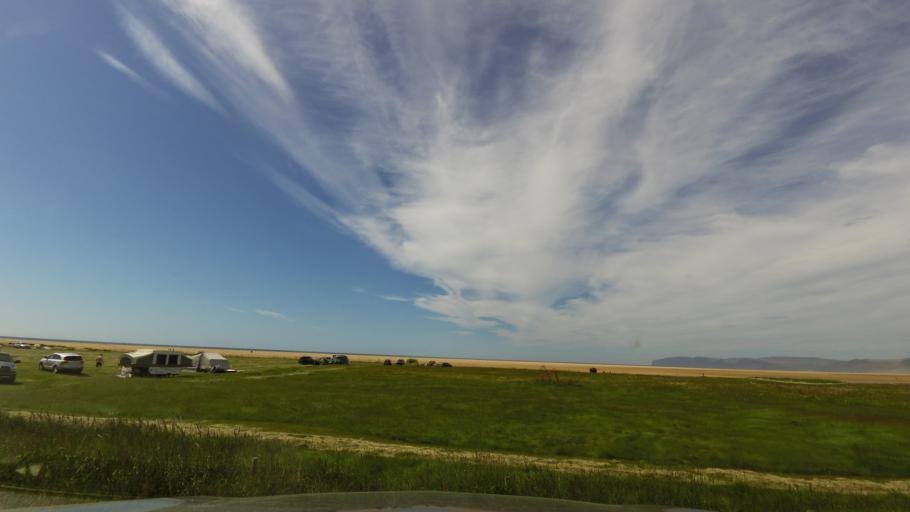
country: IS
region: West
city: Olafsvik
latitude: 65.4456
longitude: -23.9528
